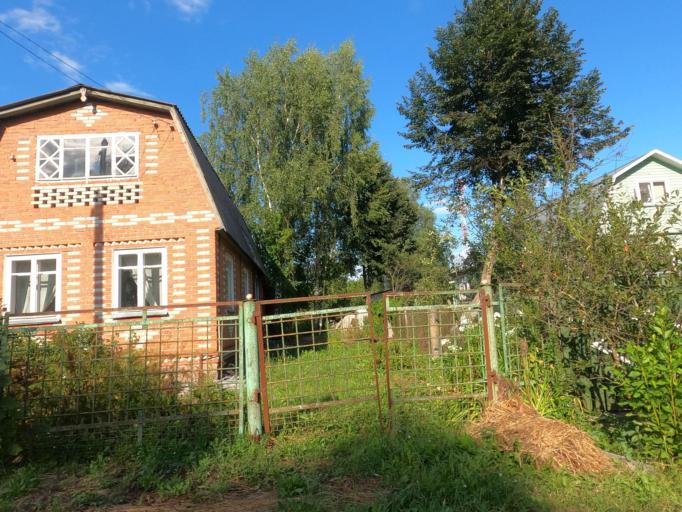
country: RU
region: Moskovskaya
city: Konobeyevo
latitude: 55.4123
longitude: 38.6956
